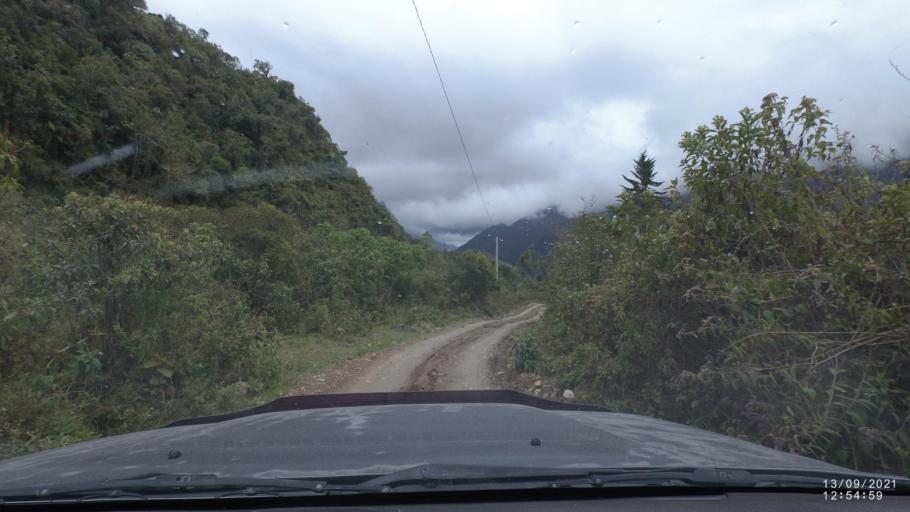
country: BO
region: Cochabamba
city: Colomi
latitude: -17.2428
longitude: -65.8219
